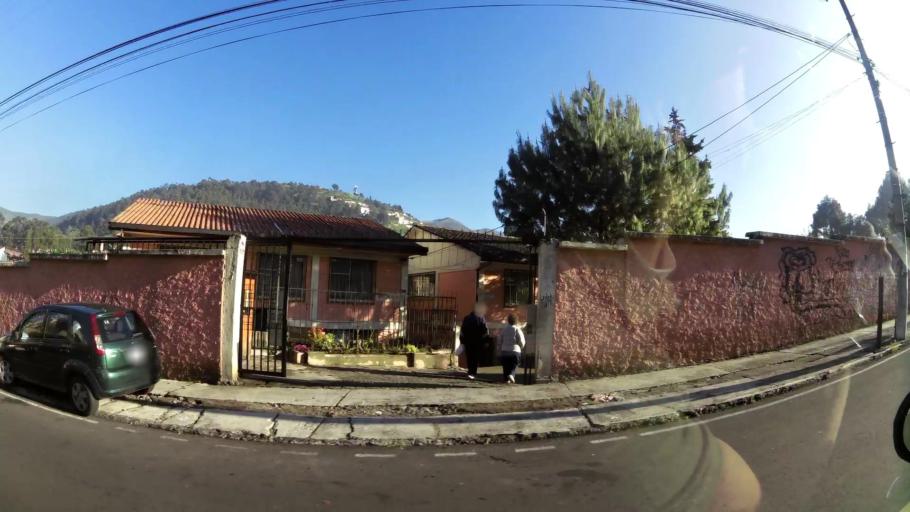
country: EC
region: Pichincha
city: Quito
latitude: -0.2360
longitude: -78.5132
